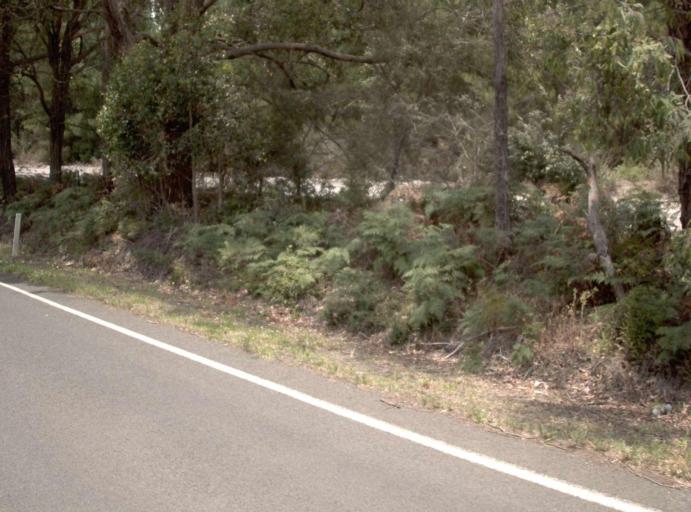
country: AU
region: Victoria
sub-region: Latrobe
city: Traralgon
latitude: -38.2614
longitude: 146.6806
